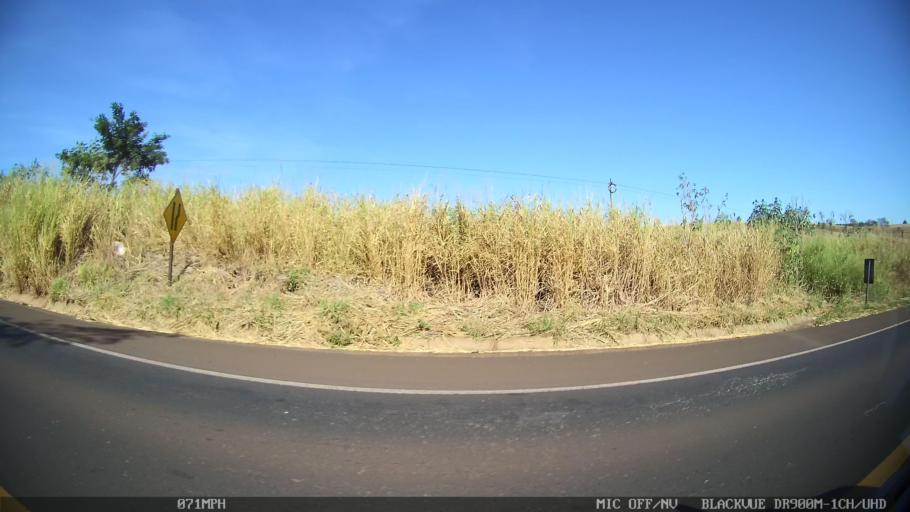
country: BR
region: Sao Paulo
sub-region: Barretos
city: Barretos
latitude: -20.6028
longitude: -48.7320
